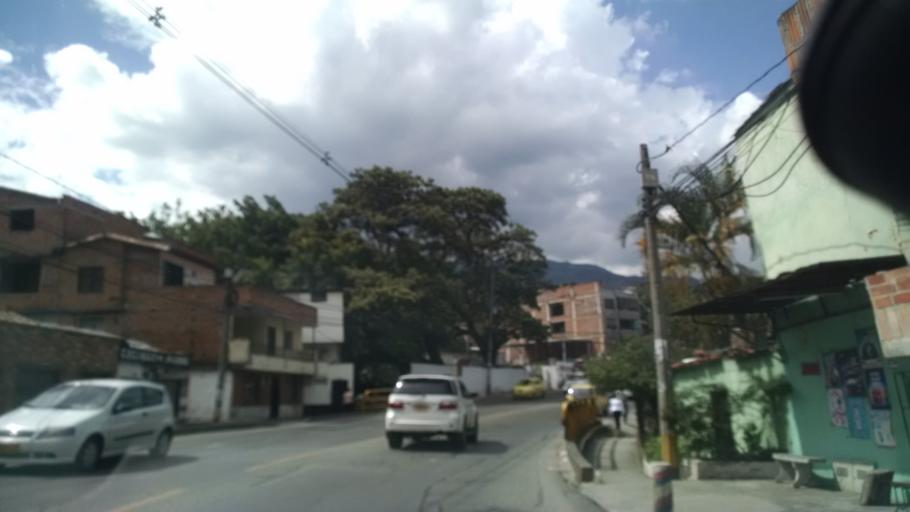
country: CO
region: Antioquia
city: Medellin
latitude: 6.2722
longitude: -75.5796
